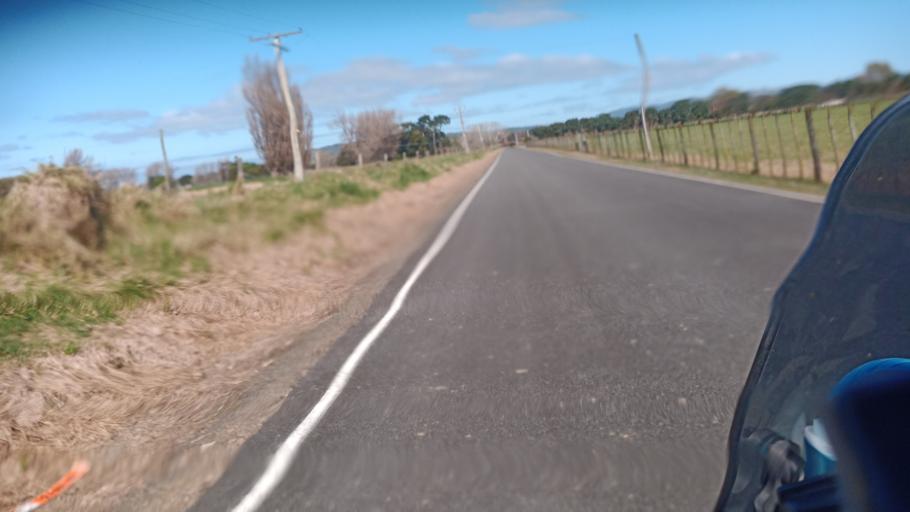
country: NZ
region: Gisborne
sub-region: Gisborne District
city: Gisborne
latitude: -39.0352
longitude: 177.8538
